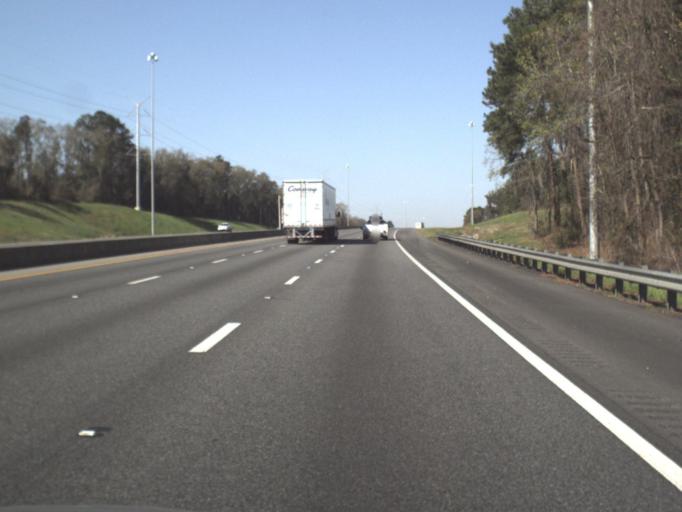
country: US
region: Florida
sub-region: Leon County
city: Tallahassee
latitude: 30.4788
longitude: -84.3270
